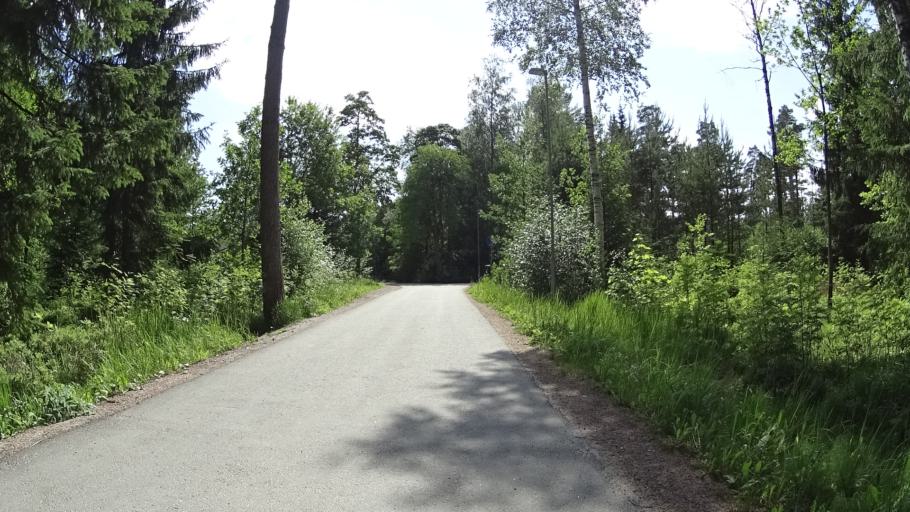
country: FI
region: Uusimaa
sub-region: Raaseporin
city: Karis
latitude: 60.0772
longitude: 23.6704
